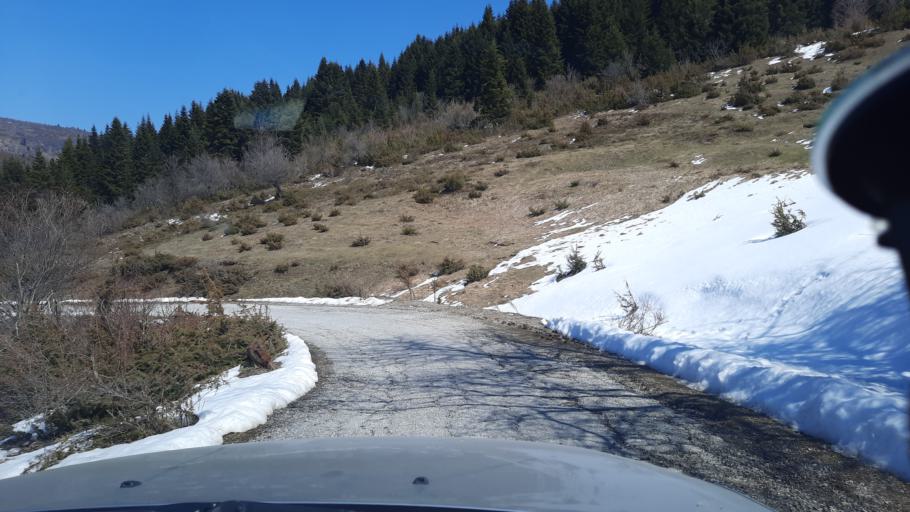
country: MK
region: Gostivar
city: Vrutok
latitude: 41.7160
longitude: 20.7262
